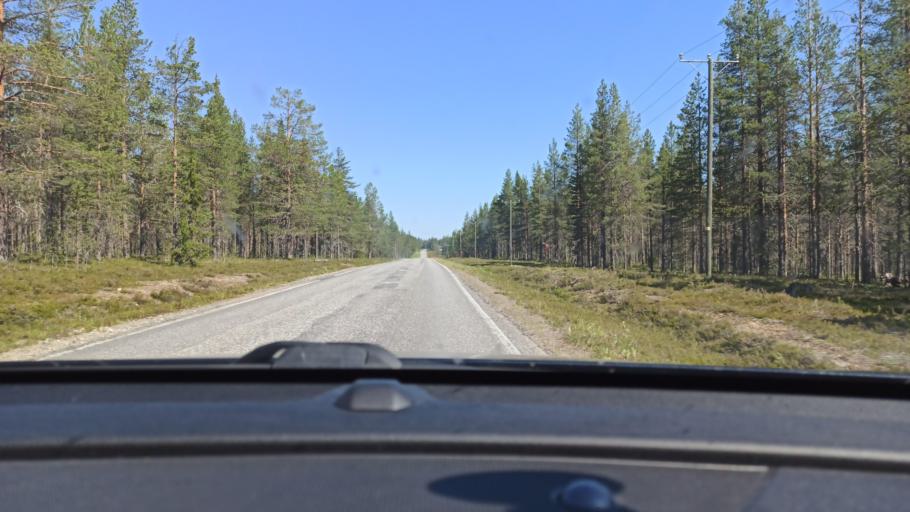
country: FI
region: Lapland
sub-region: Tunturi-Lappi
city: Kolari
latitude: 67.6483
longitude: 24.1611
